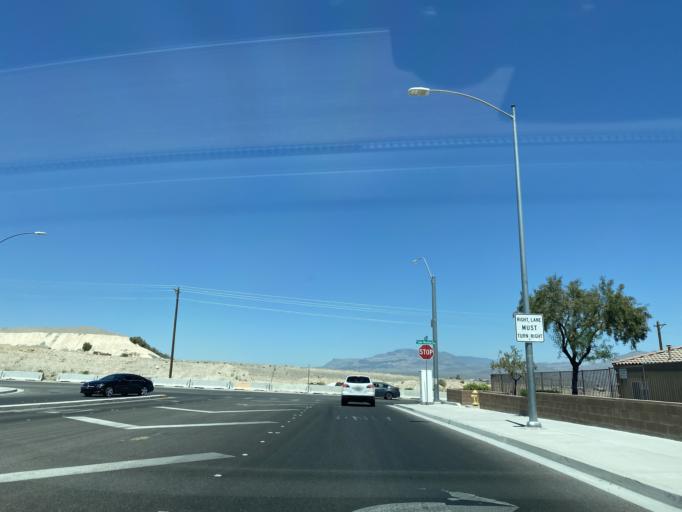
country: US
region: Nevada
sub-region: Clark County
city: Summerlin South
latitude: 36.2472
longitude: -115.3274
